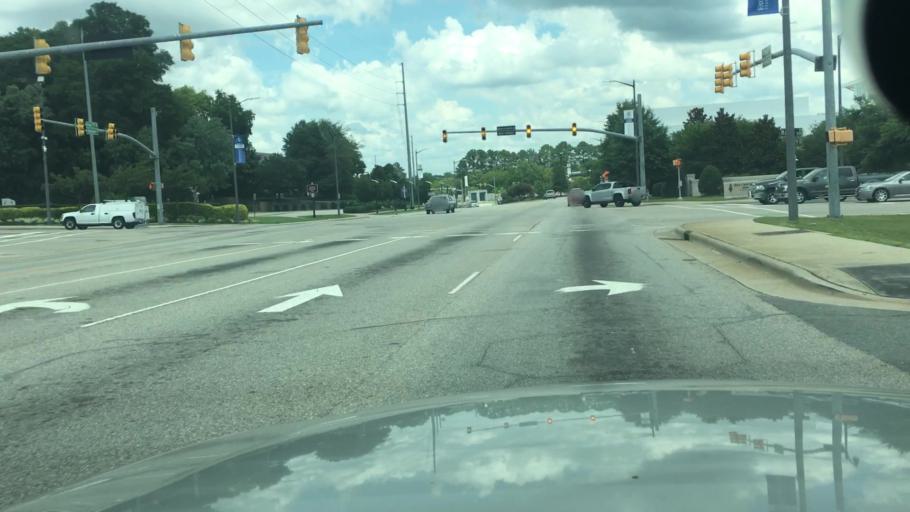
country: US
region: North Carolina
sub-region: Cumberland County
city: Fayetteville
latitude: 35.0551
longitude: -78.8869
